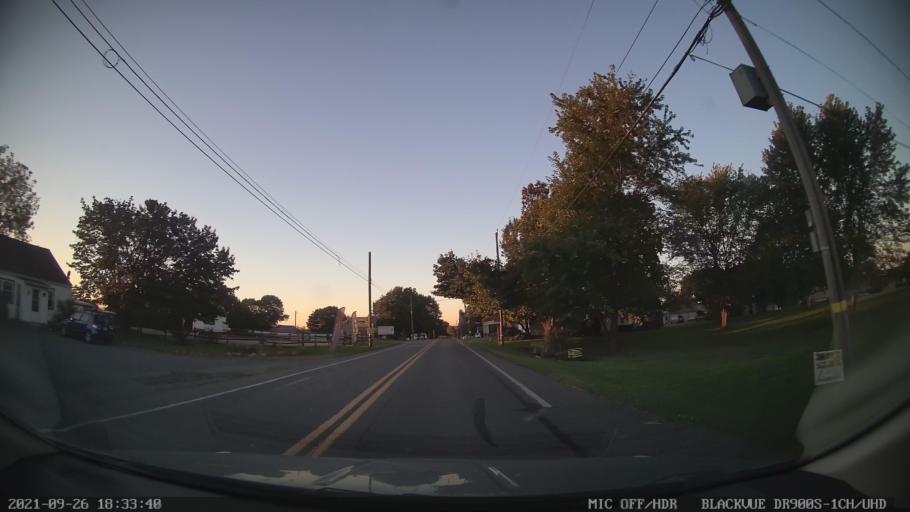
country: US
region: Pennsylvania
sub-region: Berks County
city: Kutztown
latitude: 40.5033
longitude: -75.7680
